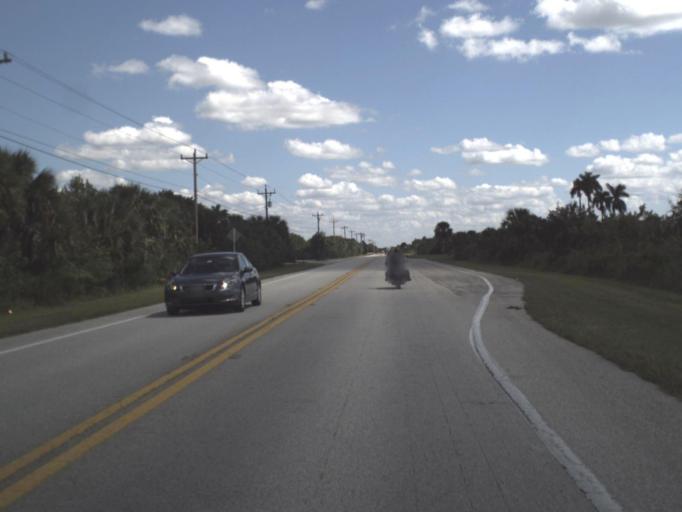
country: US
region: Florida
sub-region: Collier County
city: Marco
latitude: 25.9425
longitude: -81.4716
